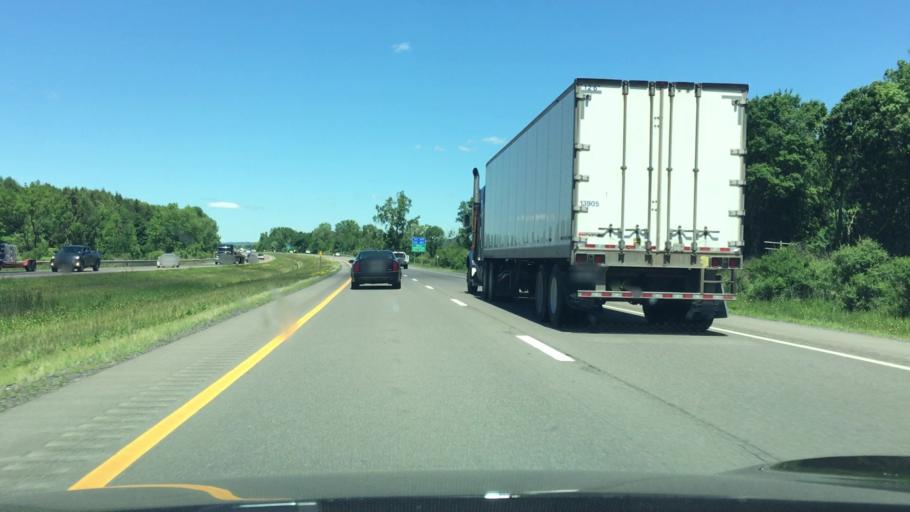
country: US
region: New York
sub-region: Cortland County
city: Homer
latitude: 42.7031
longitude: -76.1510
